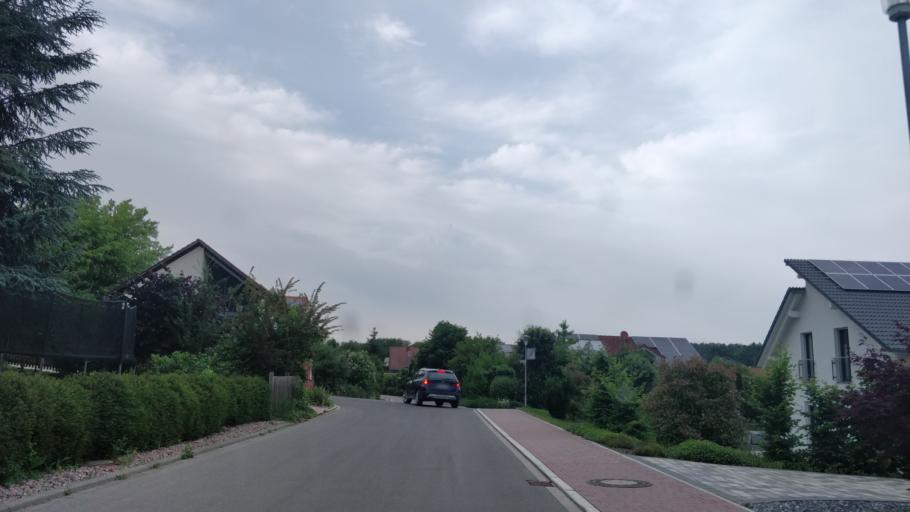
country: DE
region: Baden-Wuerttemberg
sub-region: Freiburg Region
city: Lottstetten
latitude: 47.6324
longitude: 8.5769
